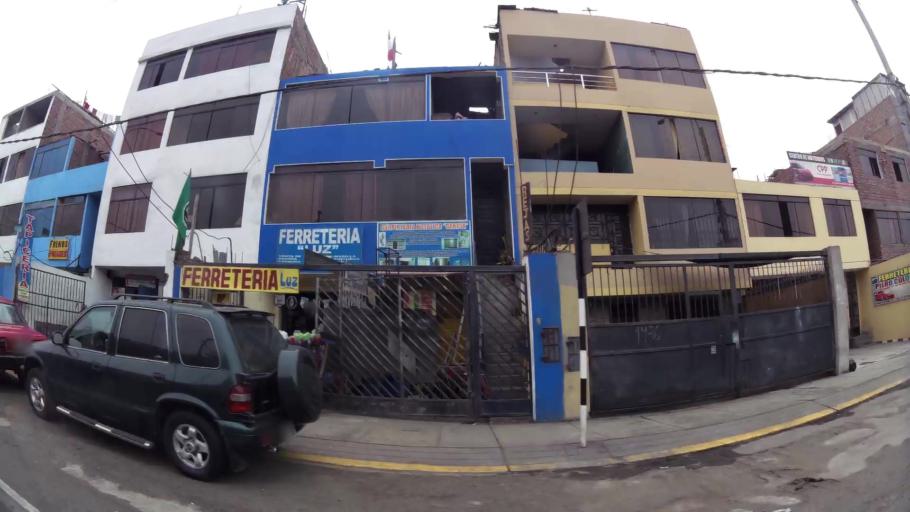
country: PE
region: Lima
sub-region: Lima
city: San Luis
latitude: -12.0839
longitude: -77.0019
